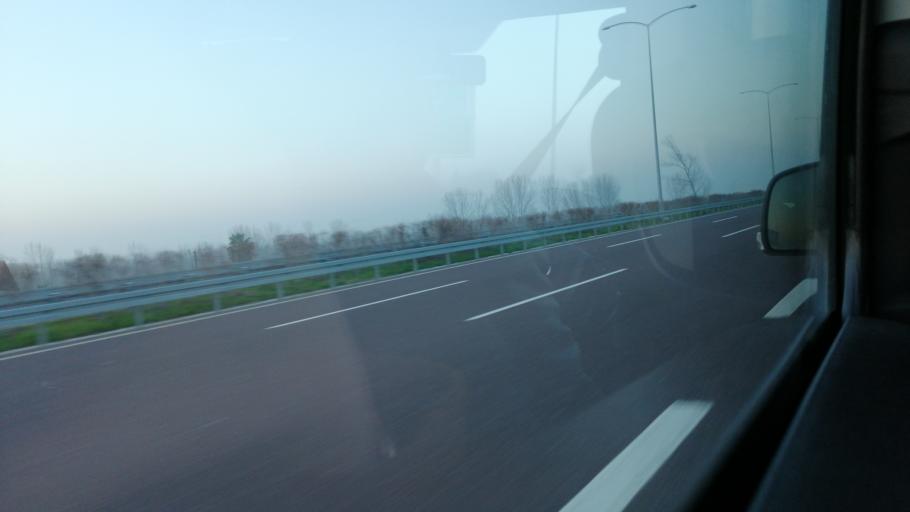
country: TR
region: Yalova
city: Altinova
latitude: 40.7025
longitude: 29.4911
